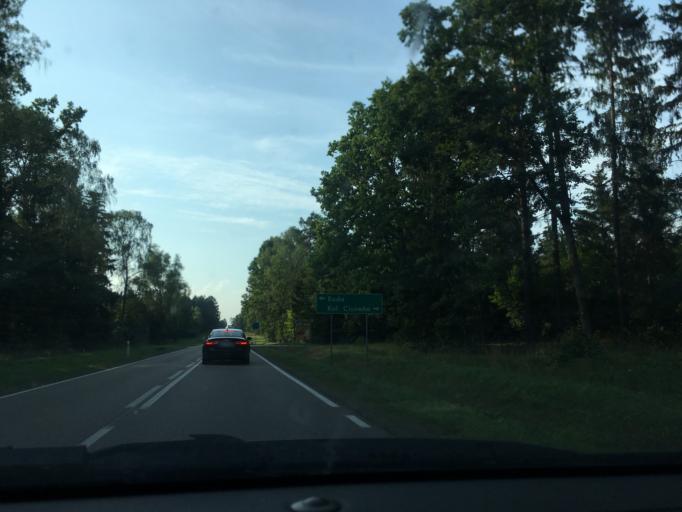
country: PL
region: Podlasie
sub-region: Powiat moniecki
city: Knyszyn
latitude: 53.2796
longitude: 22.9540
